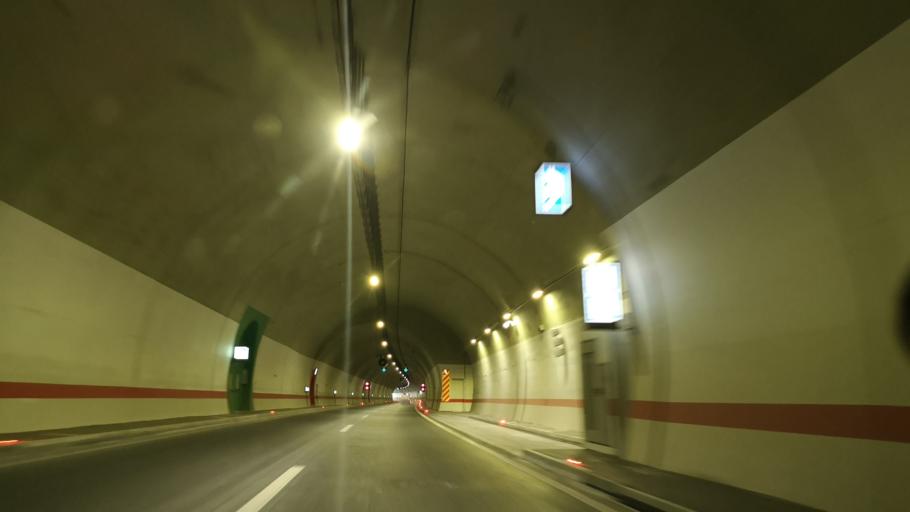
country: RS
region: Central Serbia
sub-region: Kolubarski Okrug
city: Ljig
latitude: 44.2067
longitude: 20.2641
